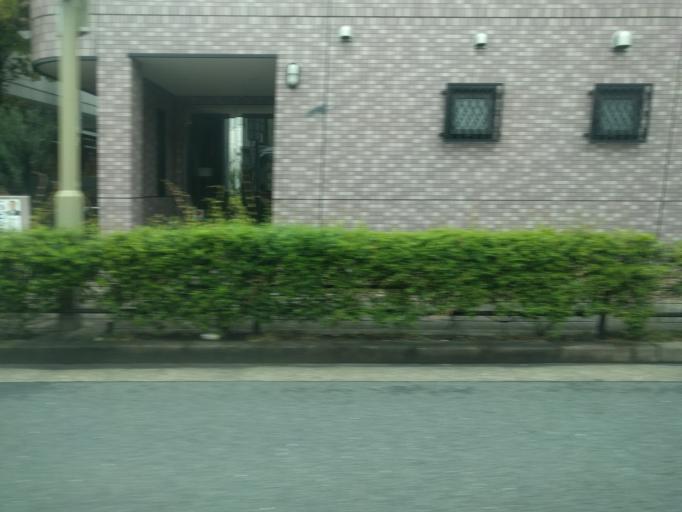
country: JP
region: Tokyo
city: Tokyo
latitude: 35.6009
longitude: 139.6728
